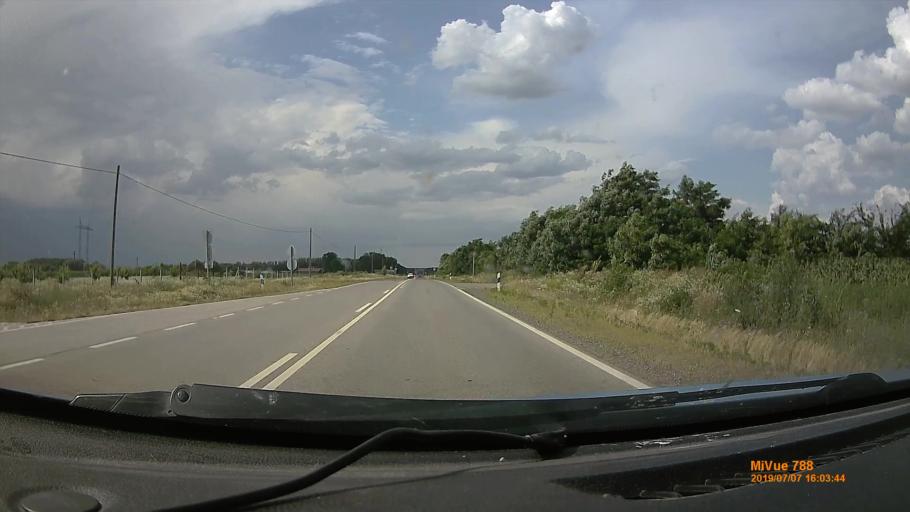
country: HU
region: Heves
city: Hatvan
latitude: 47.6428
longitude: 19.7277
